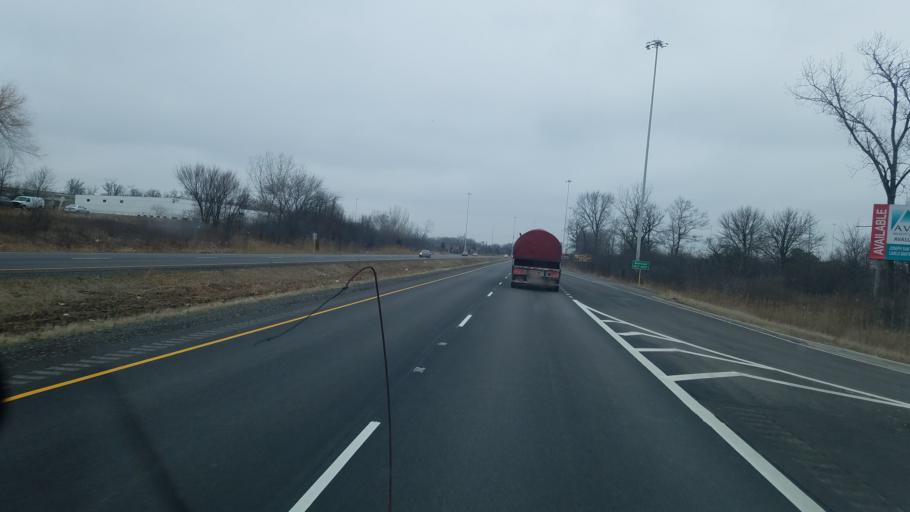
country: US
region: Illinois
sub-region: Lake County
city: Park City
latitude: 42.3427
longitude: -87.8885
